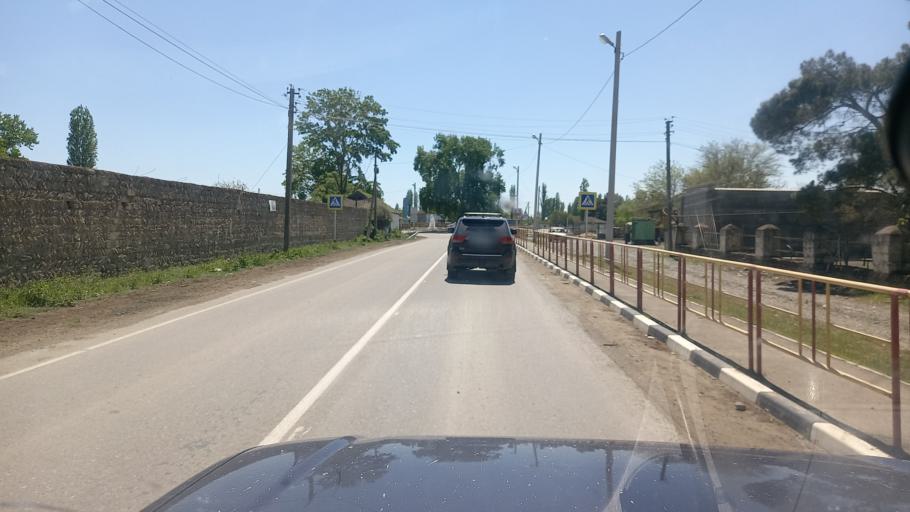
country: AZ
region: Qusar
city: Samur
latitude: 41.7264
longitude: 48.4568
